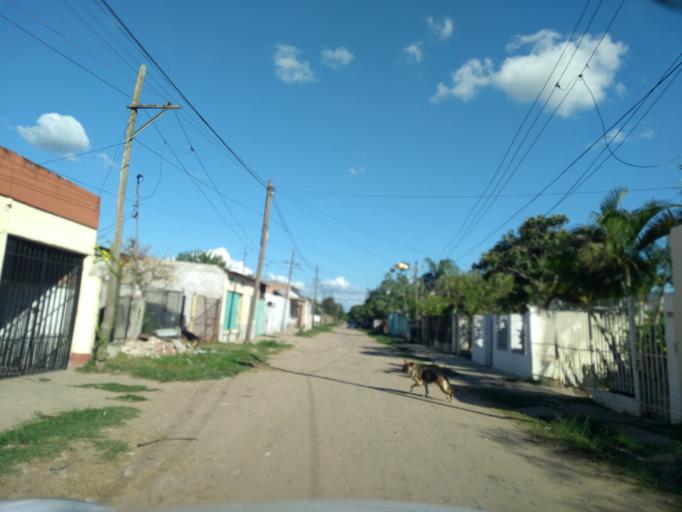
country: AR
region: Chaco
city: Resistencia
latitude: -27.4762
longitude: -58.9779
